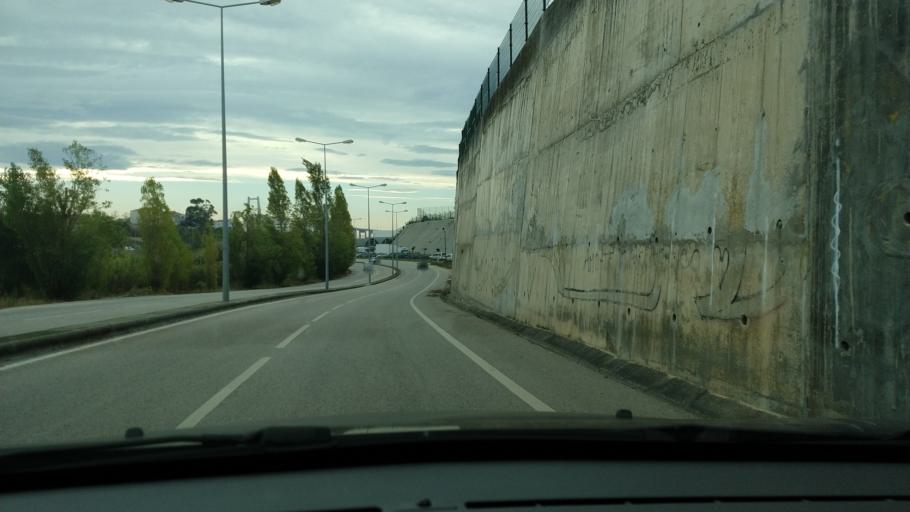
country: PT
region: Coimbra
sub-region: Figueira da Foz
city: Figueira da Foz
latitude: 40.1549
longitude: -8.8498
